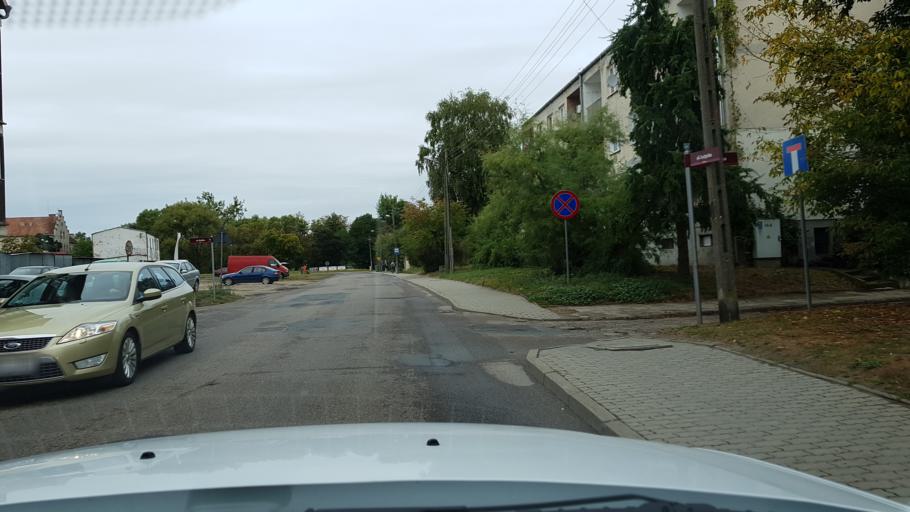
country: PL
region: West Pomeranian Voivodeship
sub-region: Powiat gryfinski
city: Chojna
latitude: 52.9645
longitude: 14.4309
